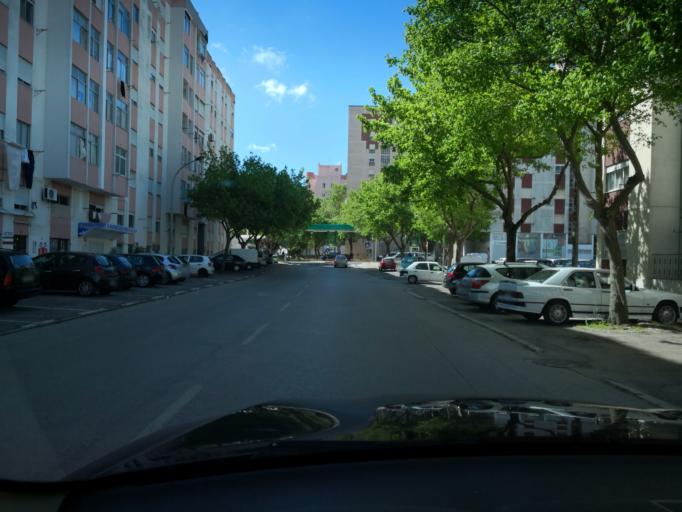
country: PT
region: Setubal
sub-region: Setubal
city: Setubal
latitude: 38.5266
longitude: -8.8702
